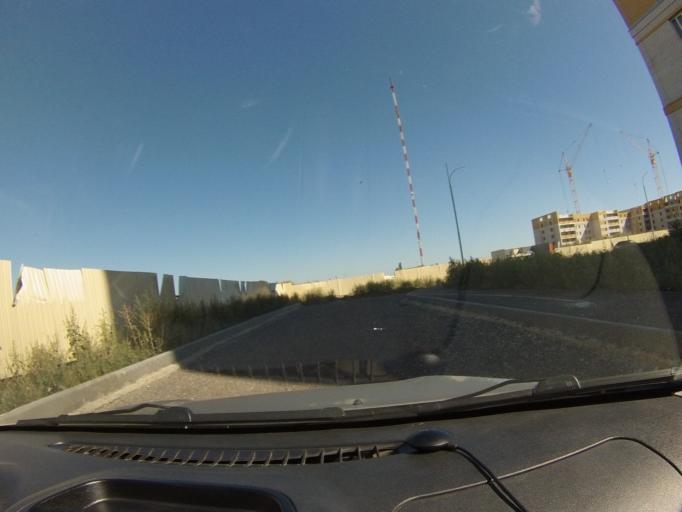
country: RU
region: Tambov
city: Tambov
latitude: 52.7797
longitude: 41.4060
